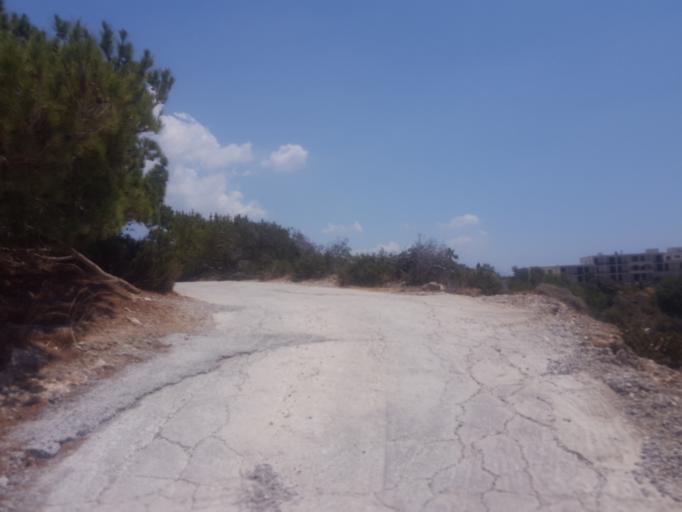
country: GR
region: Crete
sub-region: Nomos Lasithiou
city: Kato Chorio
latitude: 35.0157
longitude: 25.8453
